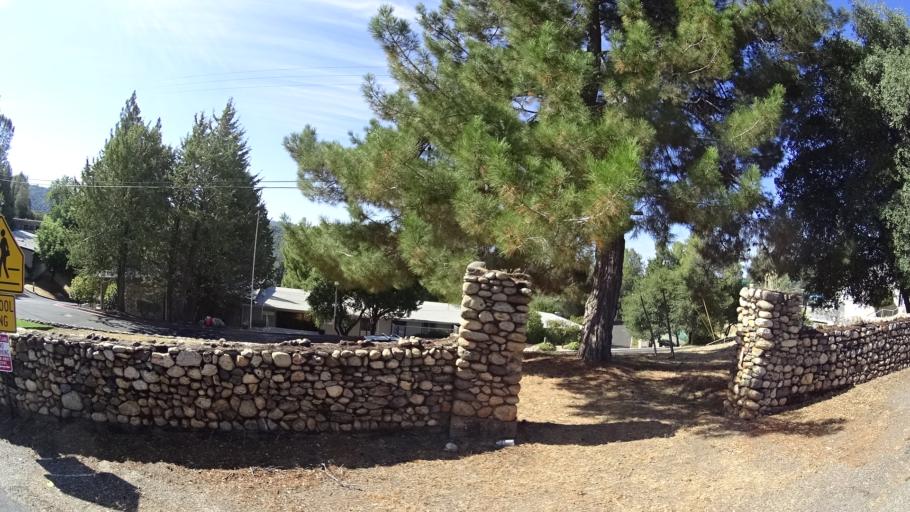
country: US
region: California
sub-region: Calaveras County
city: Mountain Ranch
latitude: 38.1739
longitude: -120.5371
